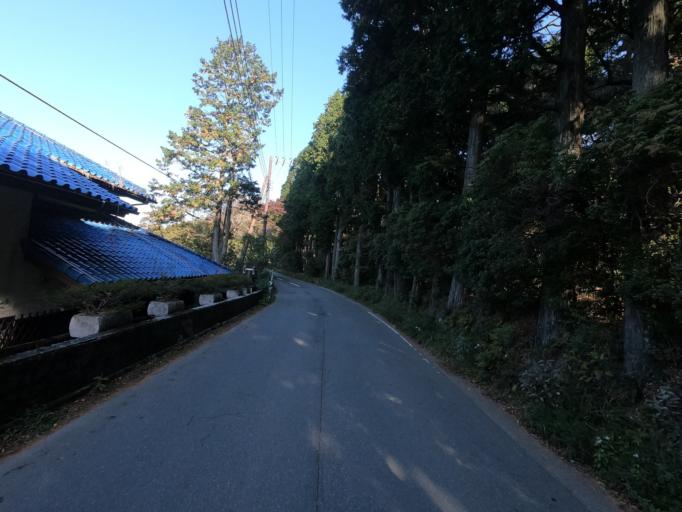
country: JP
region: Kanagawa
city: Hakone
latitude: 35.2062
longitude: 139.0176
